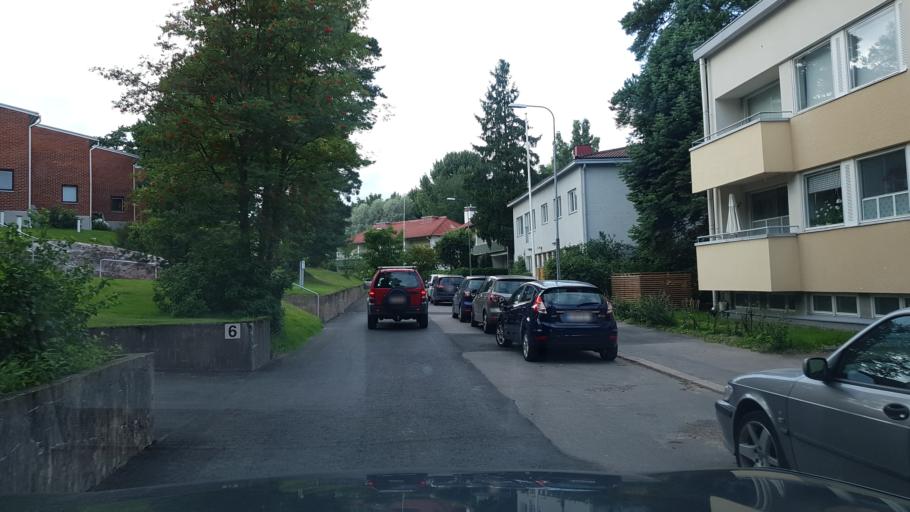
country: FI
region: Uusimaa
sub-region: Helsinki
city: Teekkarikylae
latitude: 60.2003
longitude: 24.8637
